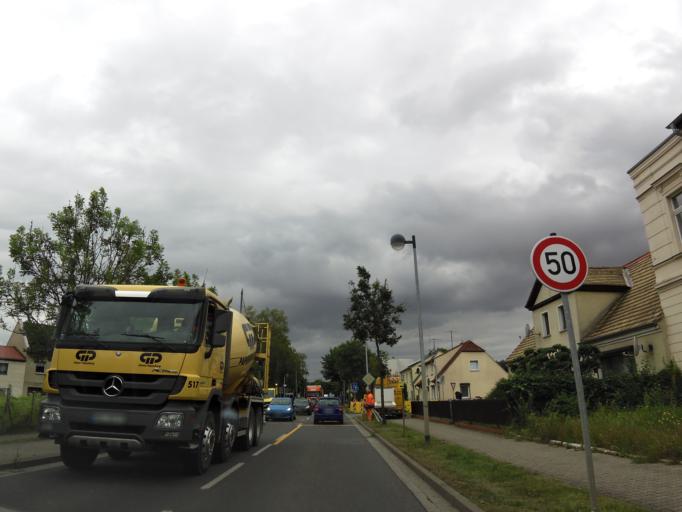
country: DE
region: Saxony
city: Markranstadt
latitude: 51.2998
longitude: 12.2174
